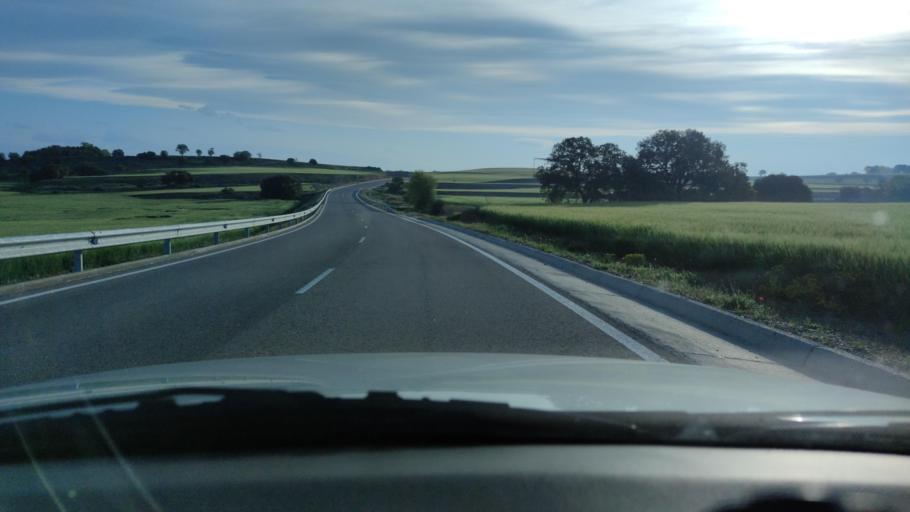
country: ES
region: Catalonia
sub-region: Provincia de Lleida
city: Castellsera
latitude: 41.7767
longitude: 1.0366
